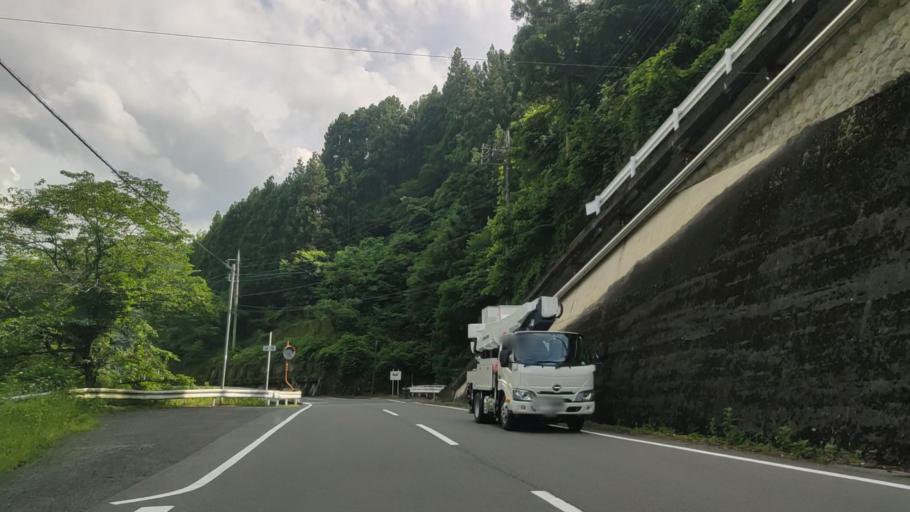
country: JP
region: Gunma
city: Tomioka
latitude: 36.1553
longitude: 138.7280
